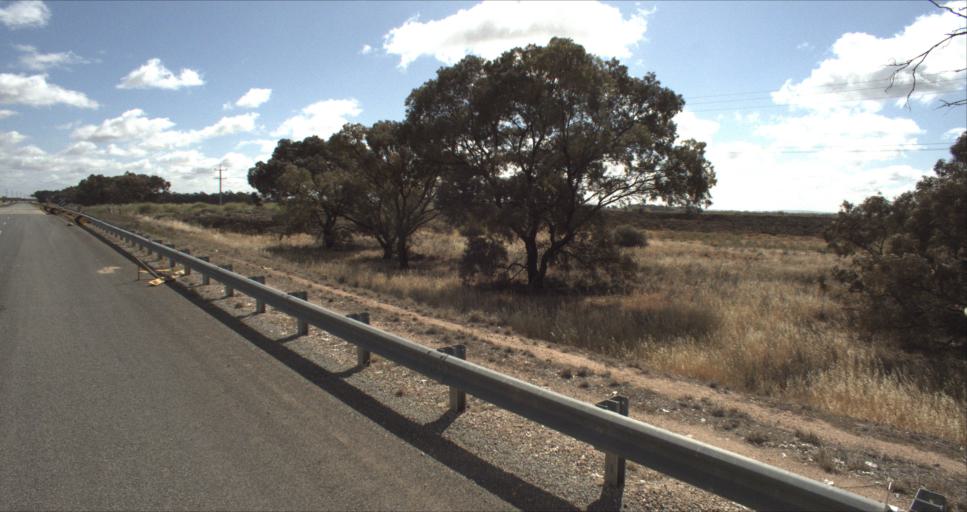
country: AU
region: New South Wales
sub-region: Murrumbidgee Shire
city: Darlington Point
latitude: -34.5537
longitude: 146.1702
